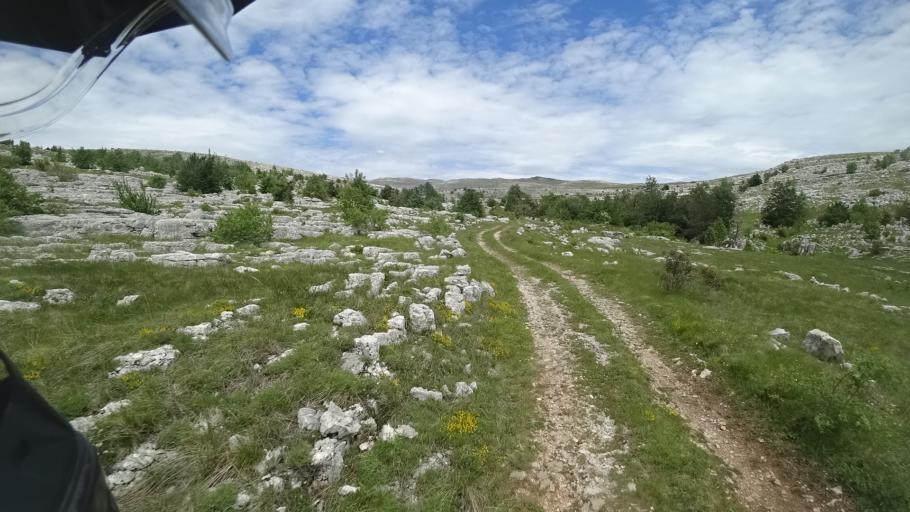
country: HR
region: Splitsko-Dalmatinska
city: Hrvace
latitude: 43.8941
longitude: 16.5864
